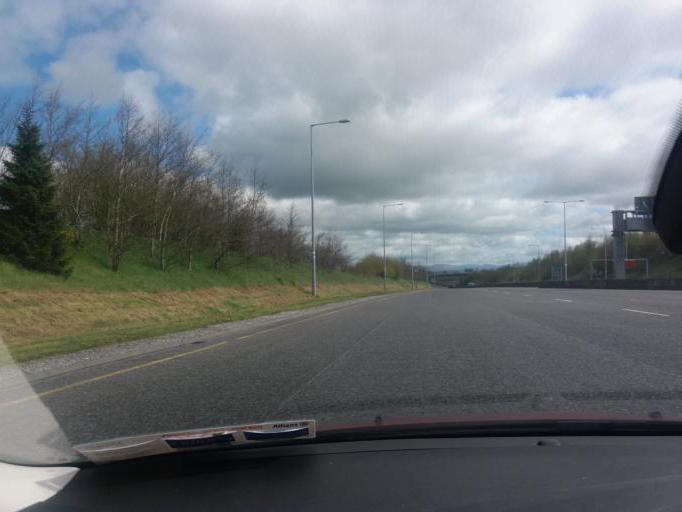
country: IE
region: Munster
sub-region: County Cork
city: Watergrasshill
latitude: 52.0282
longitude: -8.3271
